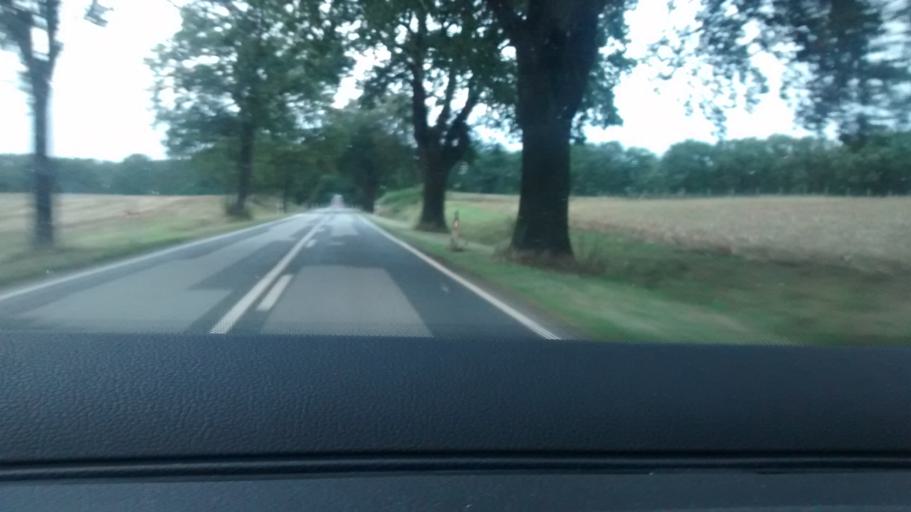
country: DE
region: Mecklenburg-Vorpommern
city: Lubtheen
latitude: 53.3992
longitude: 10.9827
